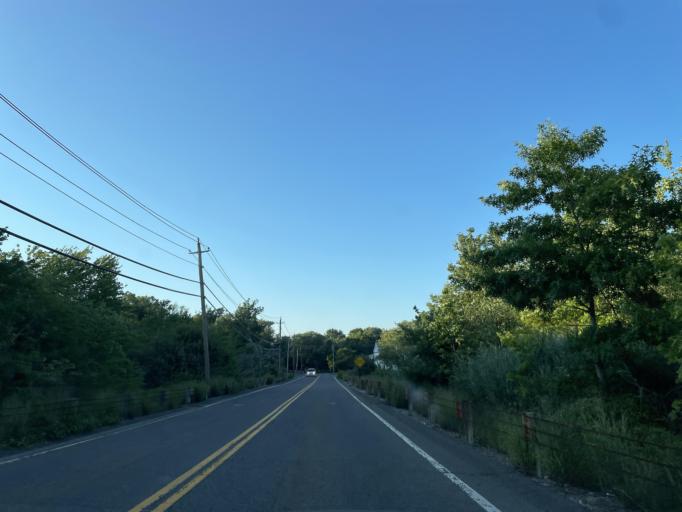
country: US
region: Massachusetts
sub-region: Plymouth County
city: Hanson
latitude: 42.0399
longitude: -70.8430
